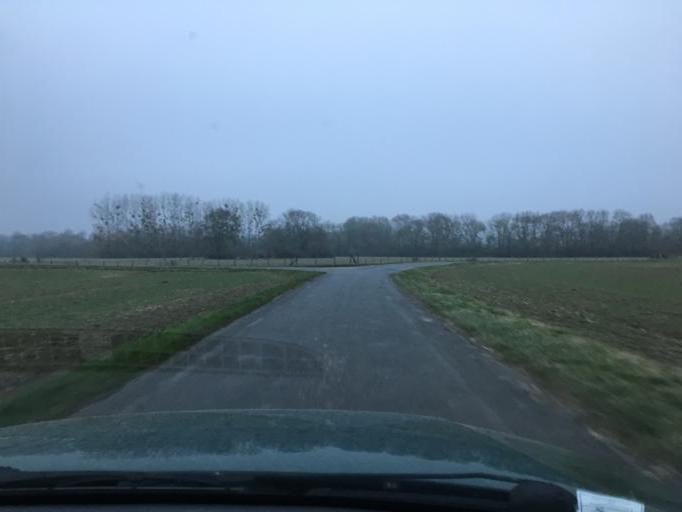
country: FR
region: Centre
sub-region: Departement du Loiret
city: Lailly-en-Val
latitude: 47.7639
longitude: 1.6647
